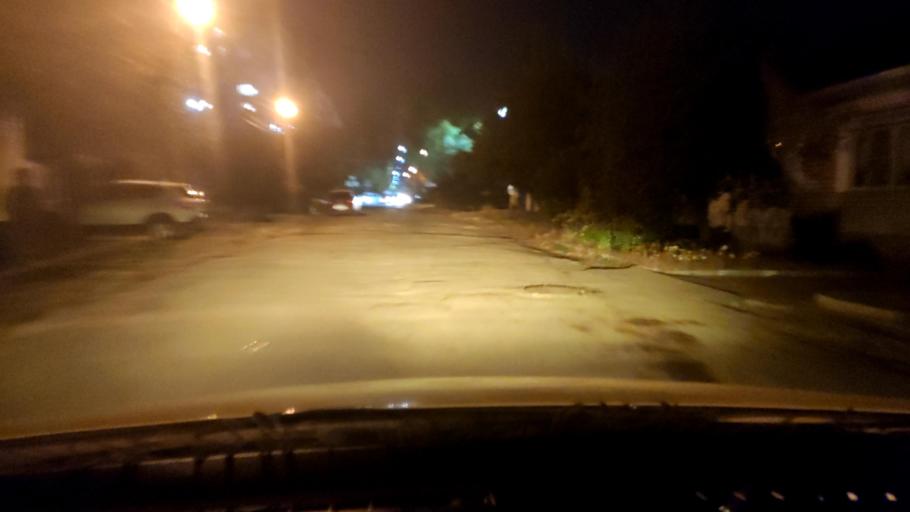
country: RU
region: Voronezj
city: Podgornoye
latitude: 51.7009
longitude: 39.1590
